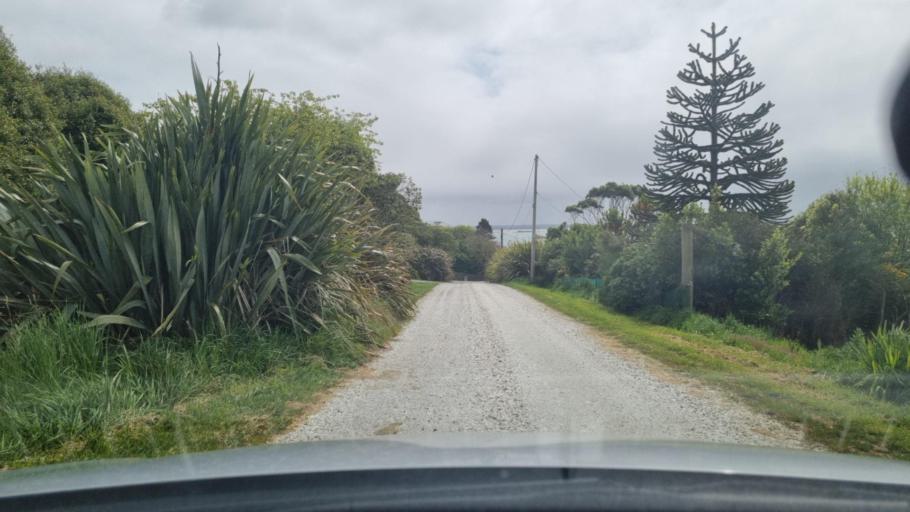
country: NZ
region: Southland
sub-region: Invercargill City
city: Bluff
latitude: -46.6077
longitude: 168.3511
